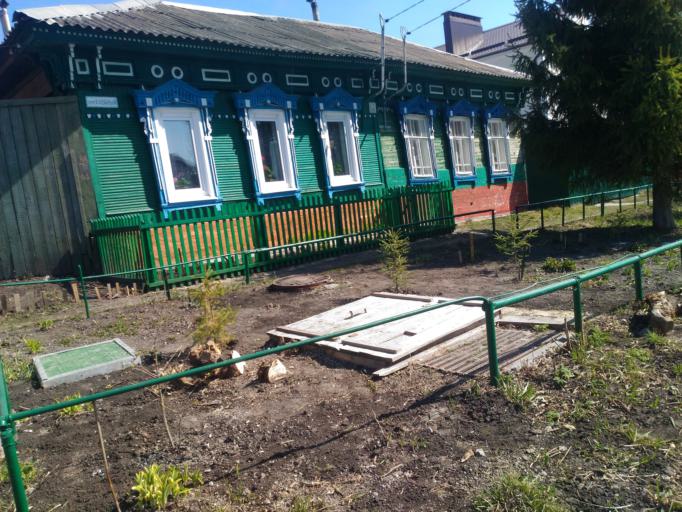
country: RU
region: Ulyanovsk
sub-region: Ulyanovskiy Rayon
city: Ulyanovsk
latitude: 54.3293
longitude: 48.3832
